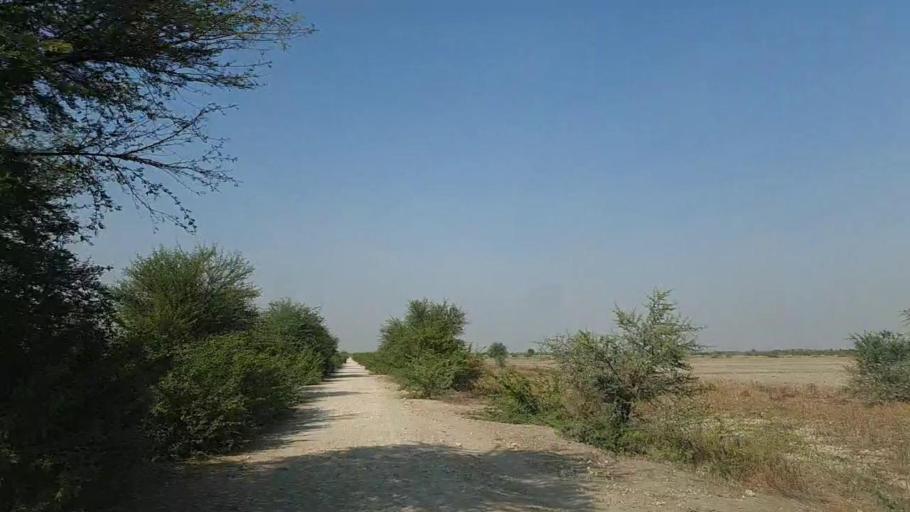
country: PK
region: Sindh
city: Naukot
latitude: 24.9120
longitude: 69.4877
